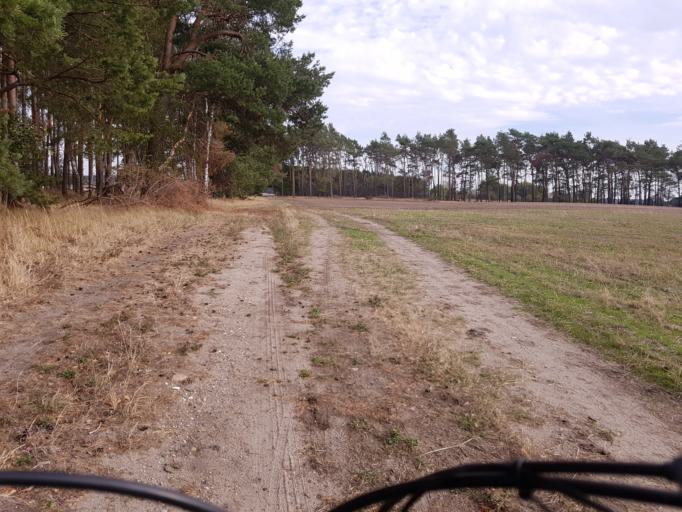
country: DE
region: Brandenburg
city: Schilda
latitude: 51.5847
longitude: 13.3695
